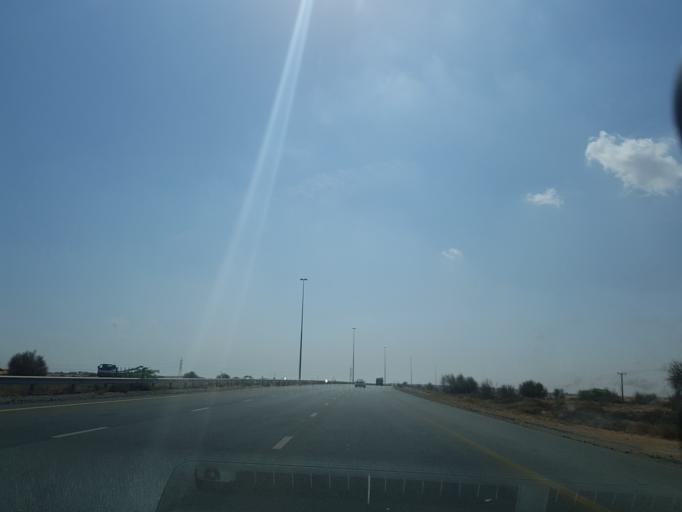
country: AE
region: Ra's al Khaymah
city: Ras al-Khaimah
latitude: 25.6826
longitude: 55.8831
